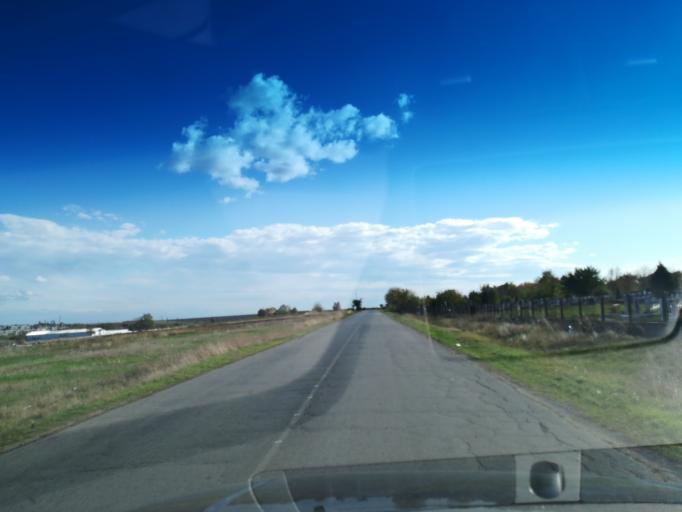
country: BG
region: Stara Zagora
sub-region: Obshtina Chirpan
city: Chirpan
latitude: 42.1995
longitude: 25.3105
